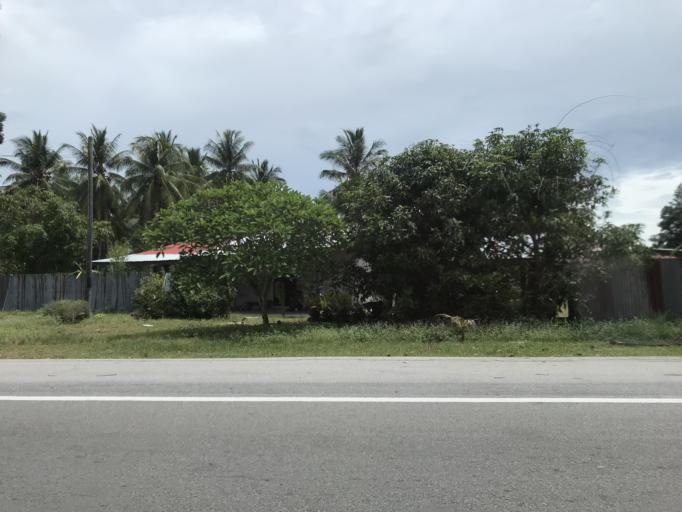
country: MY
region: Kelantan
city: Tumpat
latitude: 6.1788
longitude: 102.1802
